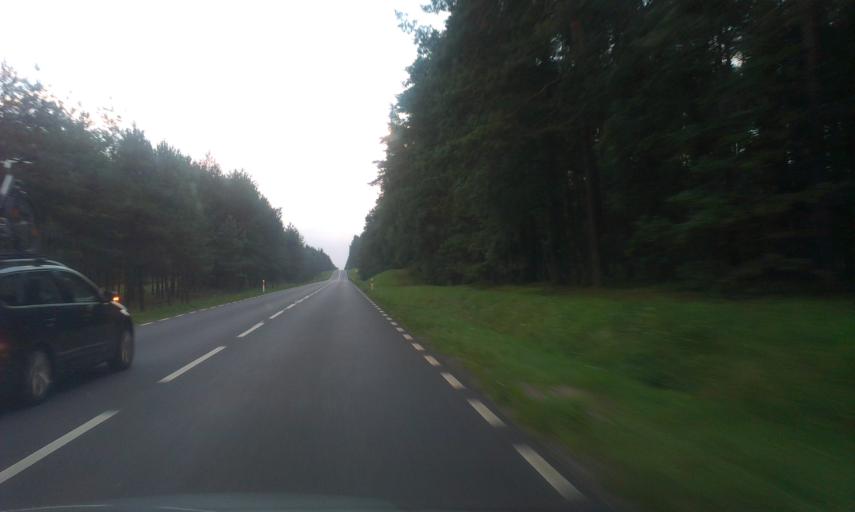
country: PL
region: West Pomeranian Voivodeship
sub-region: Powiat koszalinski
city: Sianow
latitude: 54.1071
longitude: 16.3370
